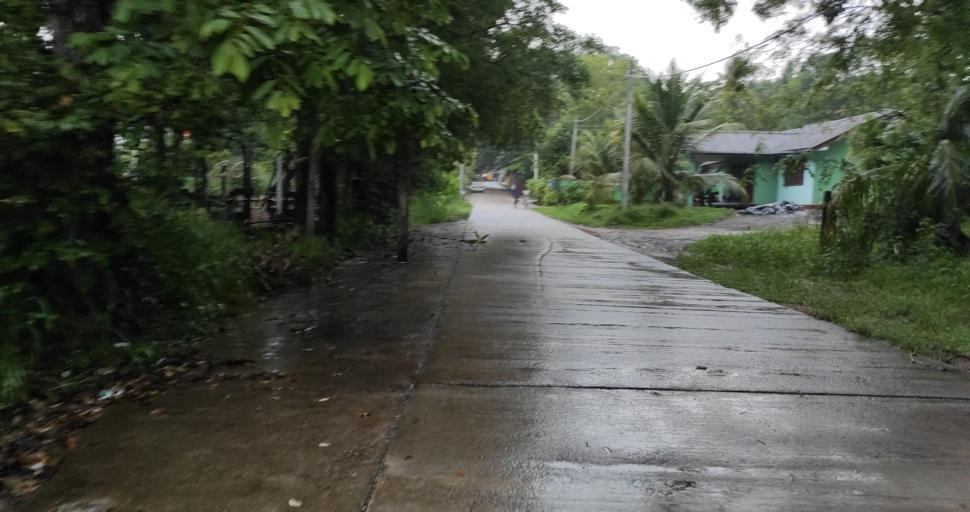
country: LK
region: Eastern Province
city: Trincomalee
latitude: 8.3651
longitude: 81.0040
